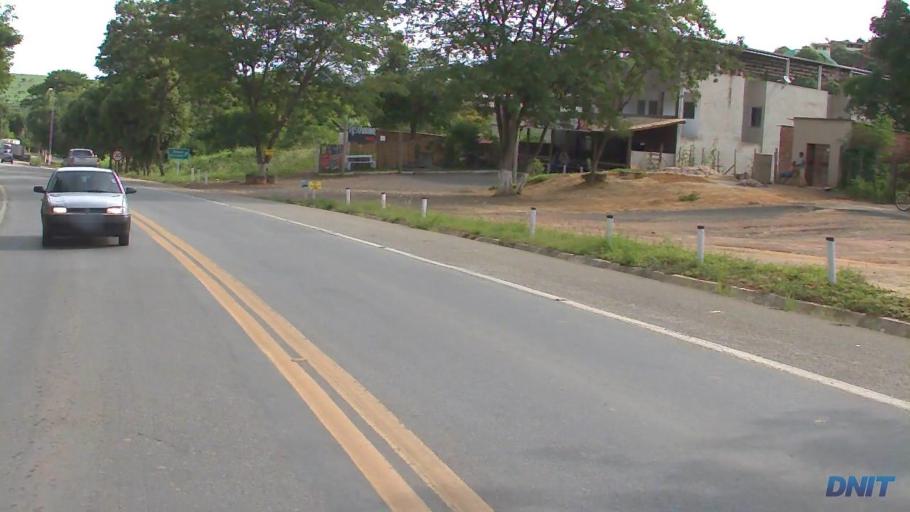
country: BR
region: Minas Gerais
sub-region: Belo Oriente
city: Belo Oriente
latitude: -19.2312
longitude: -42.3277
